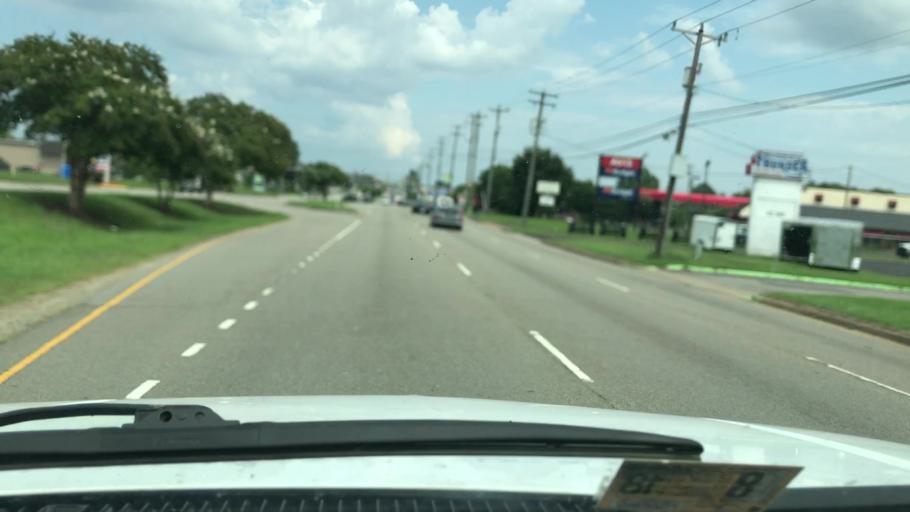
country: US
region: Virginia
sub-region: Chesterfield County
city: Bon Air
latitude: 37.4965
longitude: -77.5492
